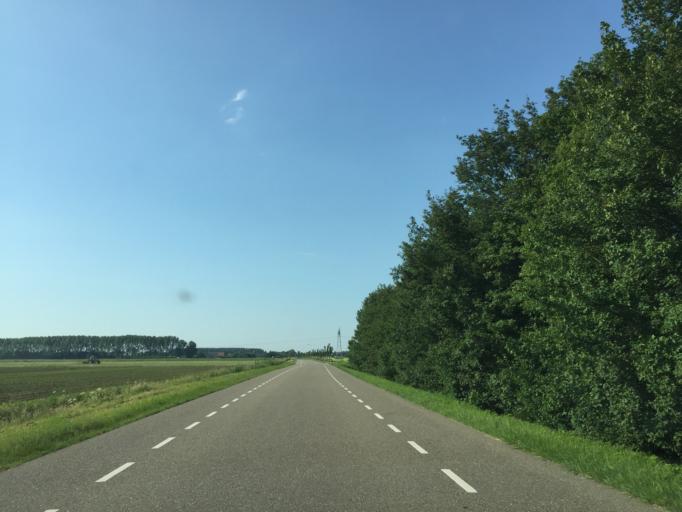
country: NL
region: Gelderland
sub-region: Gemeente Tiel
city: Tiel
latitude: 51.8662
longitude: 5.4855
